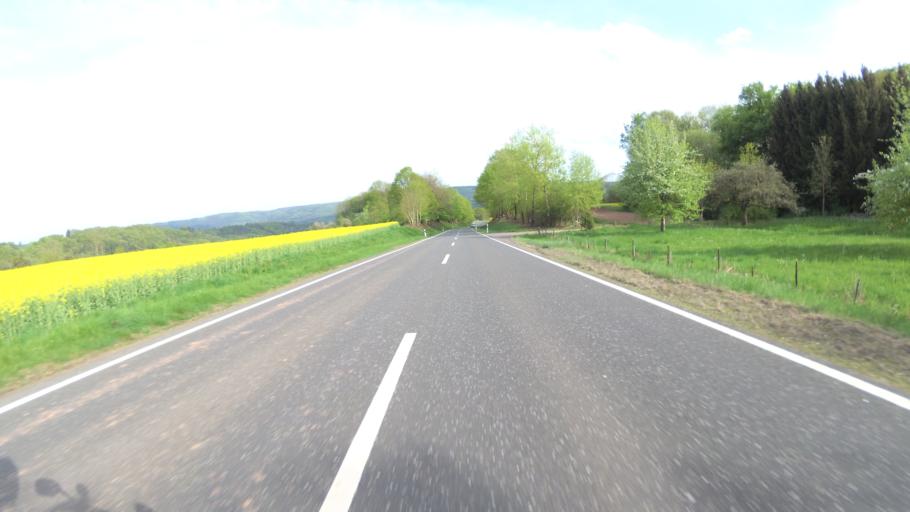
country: DE
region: Rheinland-Pfalz
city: Bausendorf
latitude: 50.0203
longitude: 7.0048
